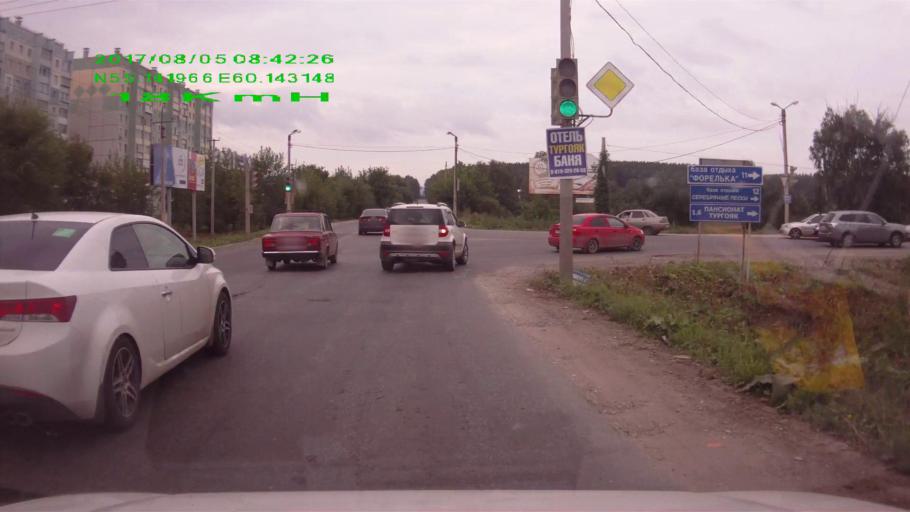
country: RU
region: Chelyabinsk
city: Turgoyak
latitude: 55.1418
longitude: 60.1432
